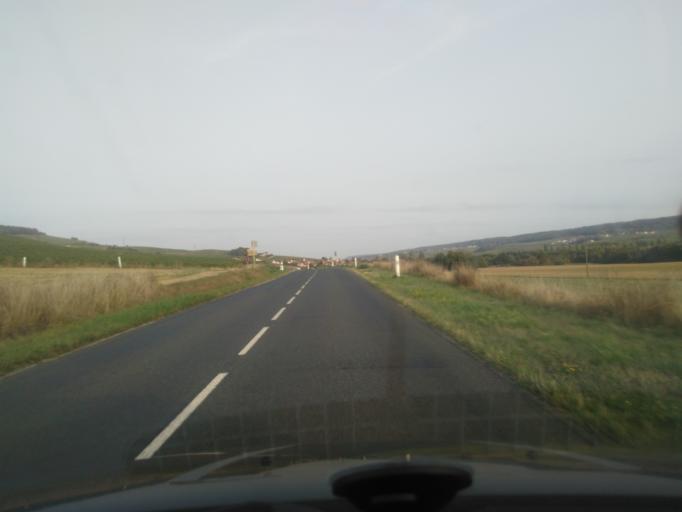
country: FR
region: Champagne-Ardenne
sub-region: Departement de la Marne
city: Mareuil-le-Port
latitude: 49.0875
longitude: 3.7836
